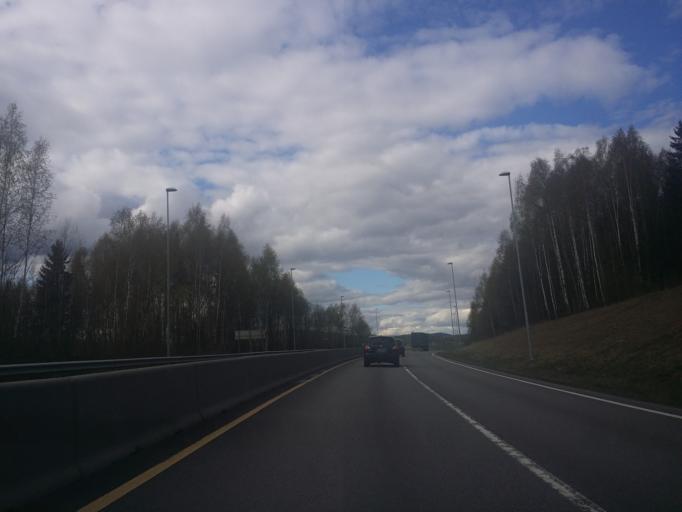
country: NO
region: Buskerud
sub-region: Ringerike
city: Honefoss
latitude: 60.1534
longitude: 10.2187
